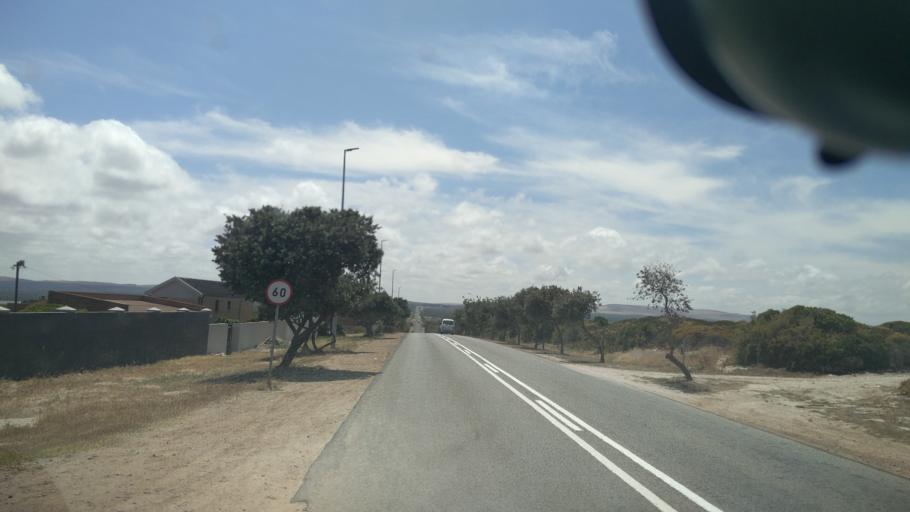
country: ZA
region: Western Cape
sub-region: City of Cape Town
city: Atlantis
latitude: -33.3444
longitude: 18.1628
